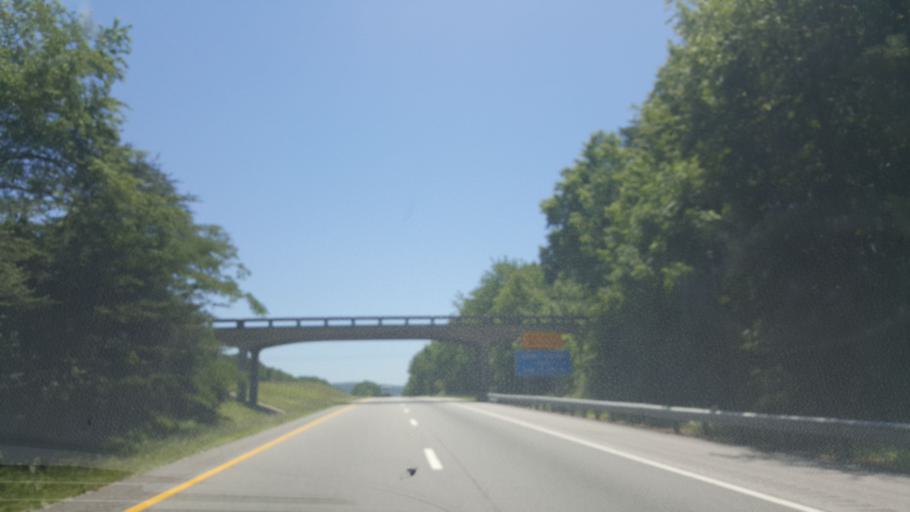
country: US
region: Tennessee
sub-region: Roane County
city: Rockwood
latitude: 35.8983
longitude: -84.7673
